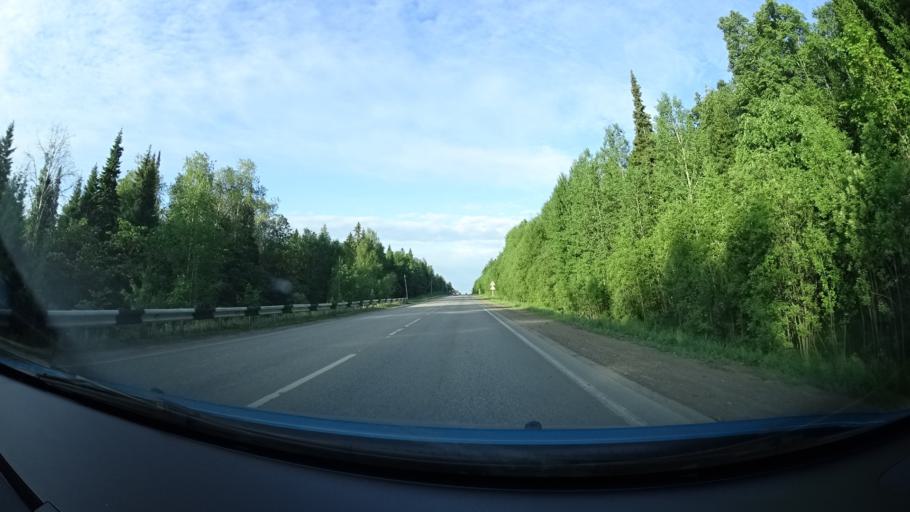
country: RU
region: Perm
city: Kultayevo
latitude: 57.8189
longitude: 55.8003
